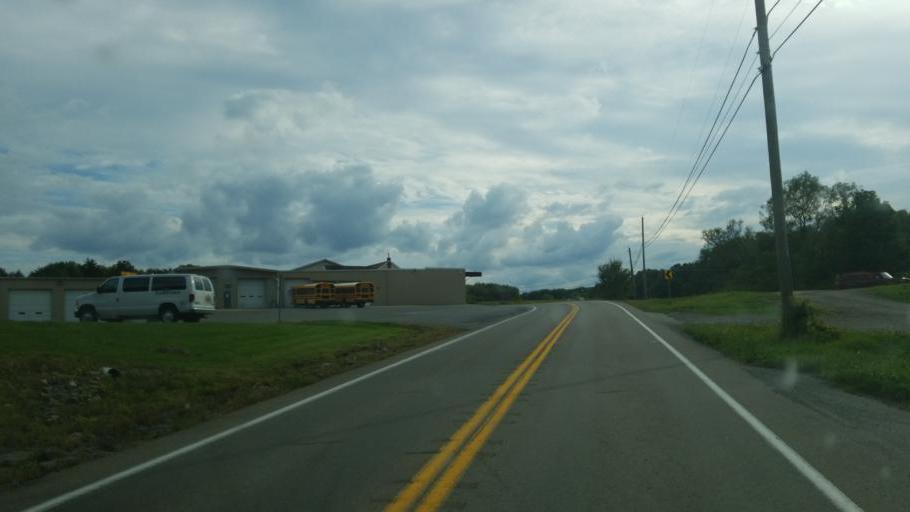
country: US
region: Pennsylvania
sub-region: Mercer County
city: Greenville
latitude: 41.4324
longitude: -80.3796
